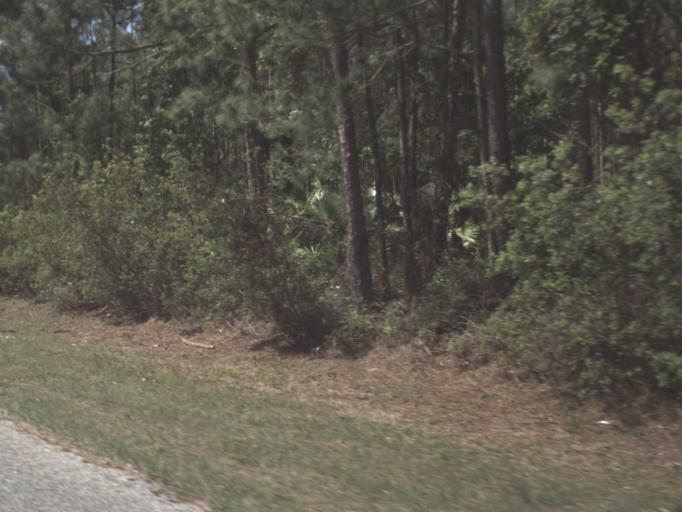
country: US
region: Florida
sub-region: Flagler County
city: Palm Coast
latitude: 29.6276
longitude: -81.2833
